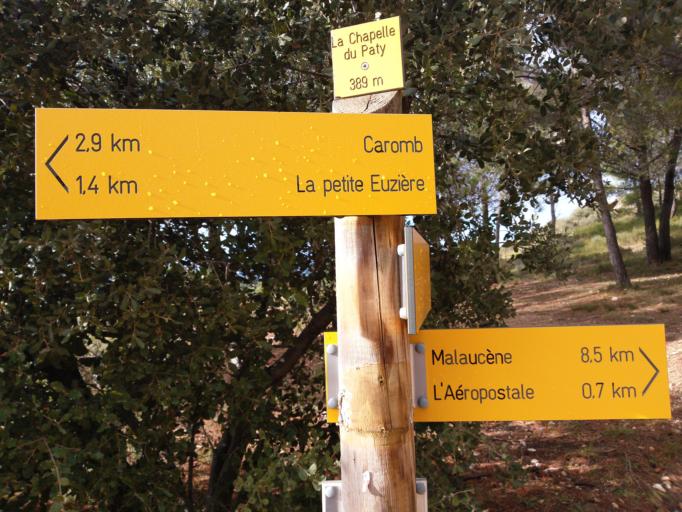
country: FR
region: Provence-Alpes-Cote d'Azur
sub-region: Departement du Vaucluse
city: Caromb
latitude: 44.1330
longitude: 5.1203
